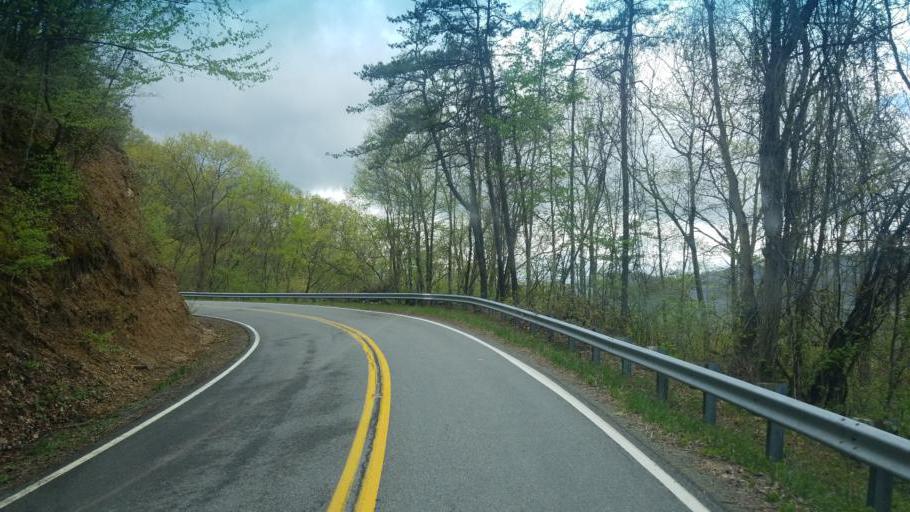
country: US
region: Virginia
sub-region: Tazewell County
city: Tazewell
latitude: 37.0035
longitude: -81.5251
